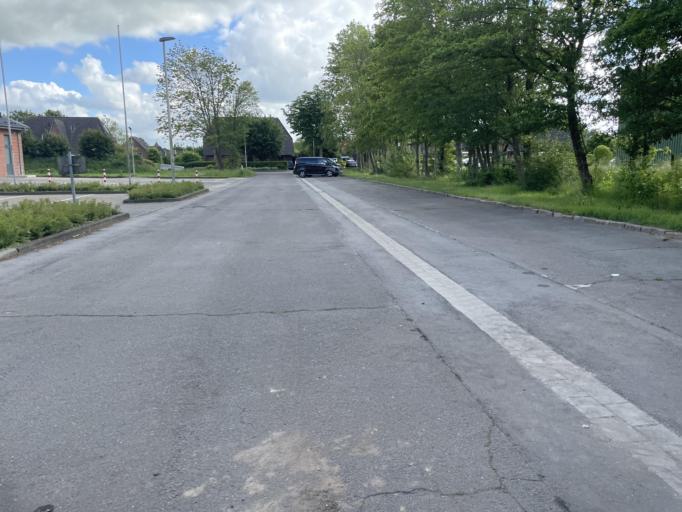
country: DE
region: Schleswig-Holstein
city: Mildstedt
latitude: 54.4680
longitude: 9.0980
